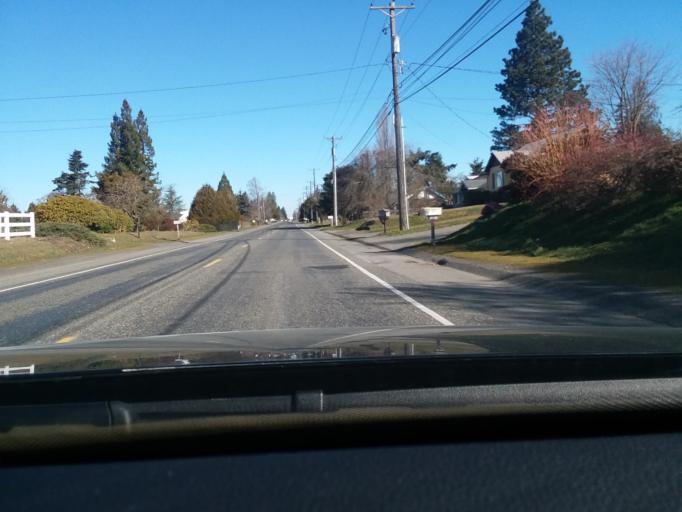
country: US
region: Washington
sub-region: Pierce County
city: Midland
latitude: 47.1642
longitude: -122.3889
